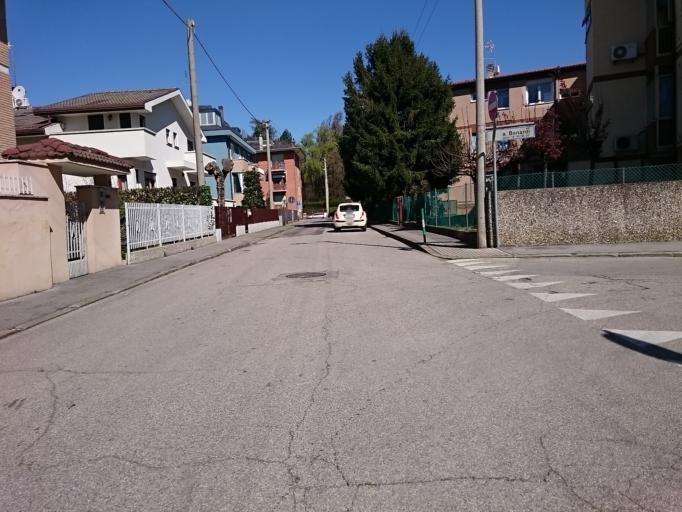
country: IT
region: Veneto
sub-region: Provincia di Padova
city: Padova
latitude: 45.3987
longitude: 11.8996
